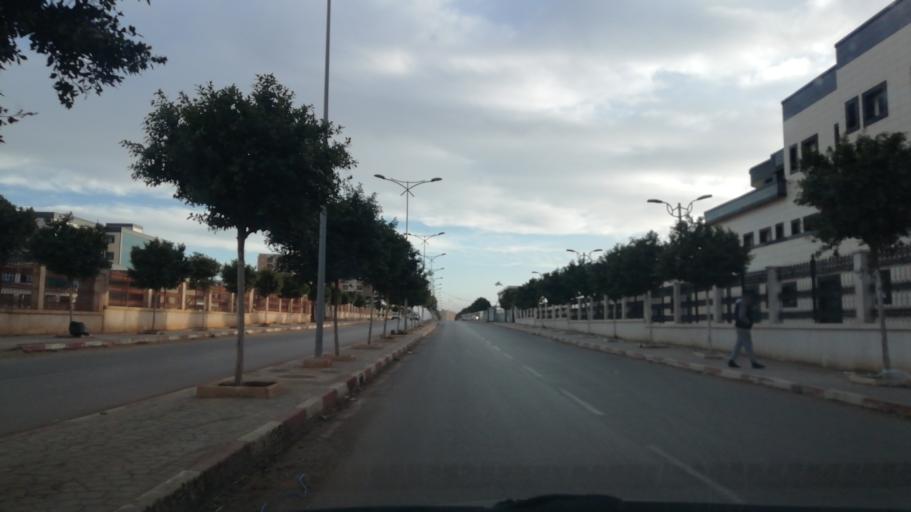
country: DZ
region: Oran
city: Bir el Djir
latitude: 35.6954
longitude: -0.5854
